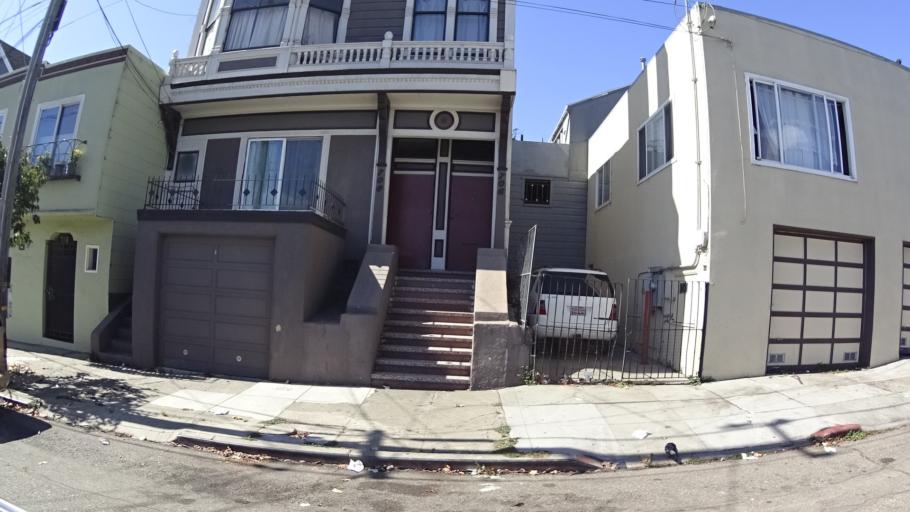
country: US
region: California
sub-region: San Francisco County
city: San Francisco
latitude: 37.7347
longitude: -122.4169
